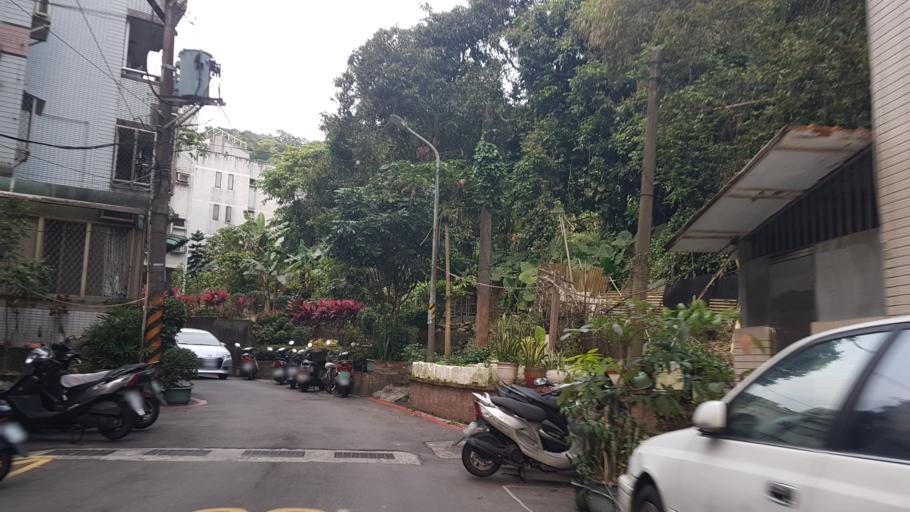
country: TW
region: Taipei
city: Taipei
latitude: 25.0049
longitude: 121.5518
